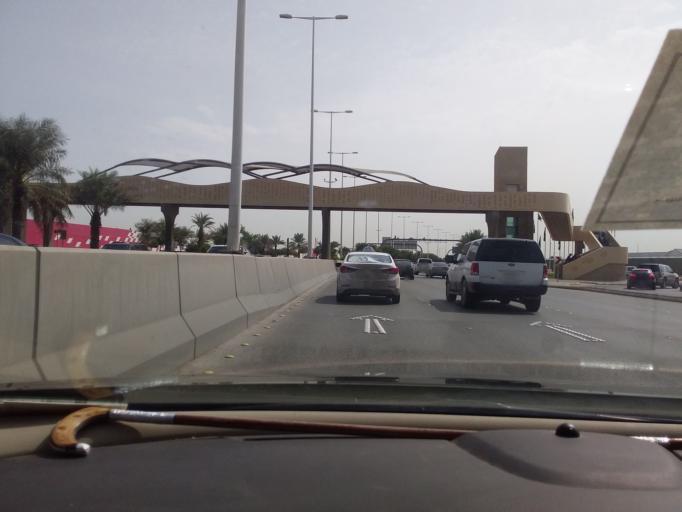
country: SA
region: Ar Riyad
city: Riyadh
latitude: 24.7336
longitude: 46.7084
